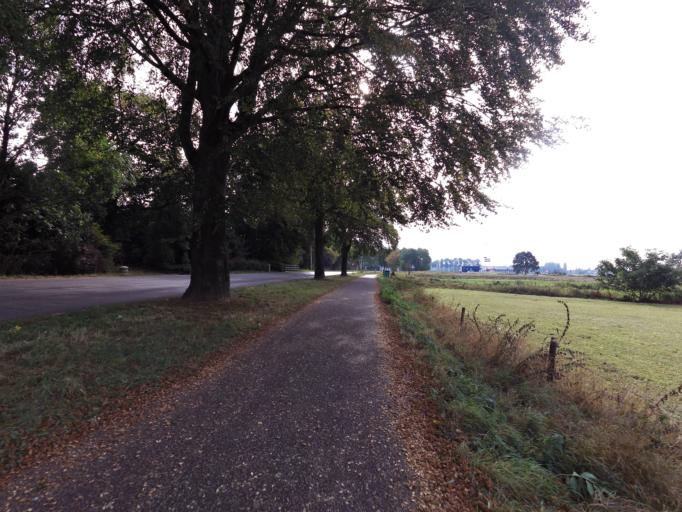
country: NL
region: Gelderland
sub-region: Oude IJsselstreek
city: Gendringen
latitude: 51.9015
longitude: 6.3894
